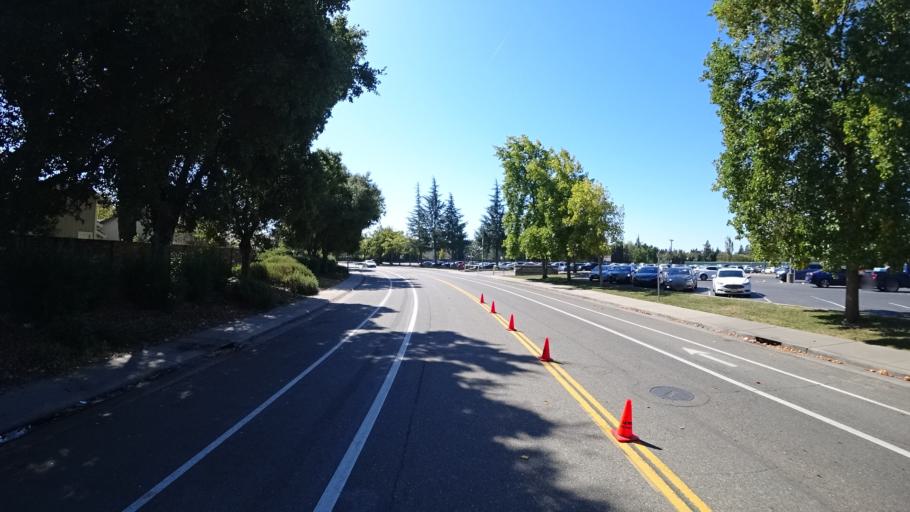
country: US
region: California
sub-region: Sacramento County
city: Laguna
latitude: 38.4287
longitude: -121.4271
